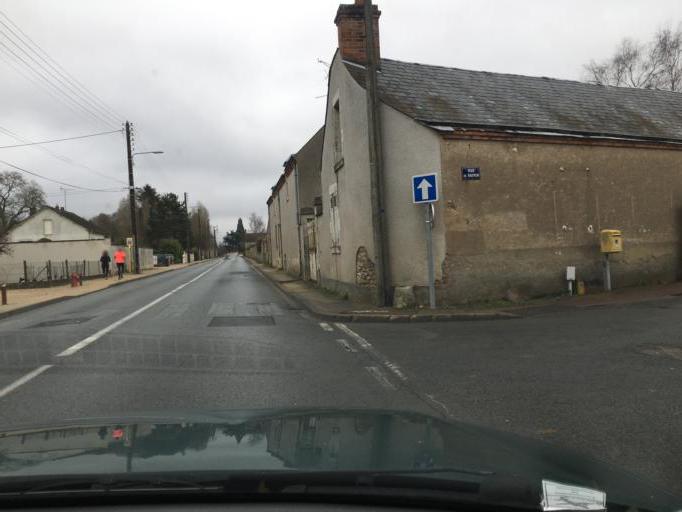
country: FR
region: Centre
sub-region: Departement du Loiret
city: Saint-Pryve-Saint-Mesmin
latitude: 47.8671
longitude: 1.8811
